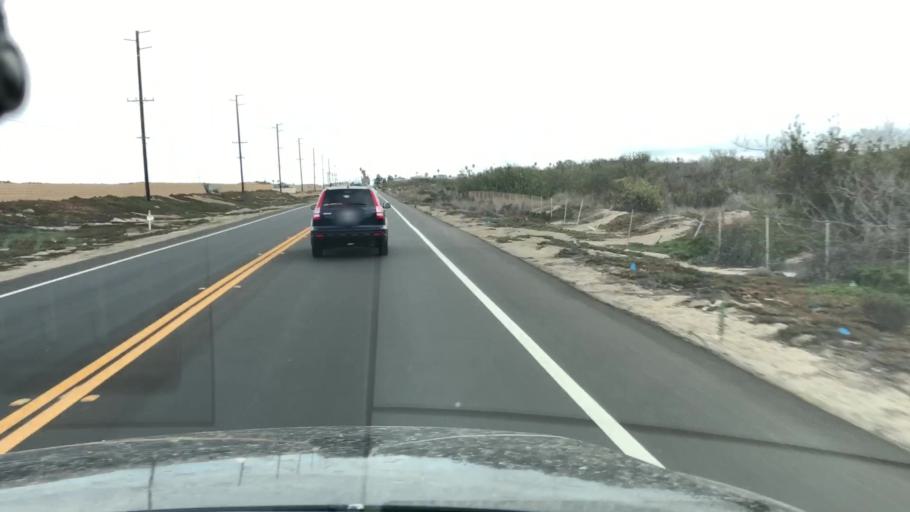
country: US
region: California
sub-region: Ventura County
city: Oxnard Shores
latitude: 34.2030
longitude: -119.2453
